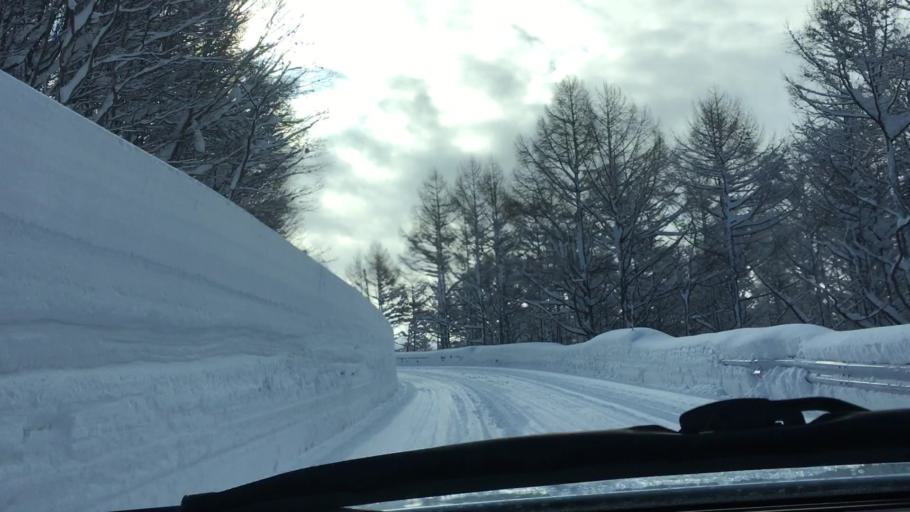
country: JP
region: Aomori
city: Aomori Shi
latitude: 40.6494
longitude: 140.7761
